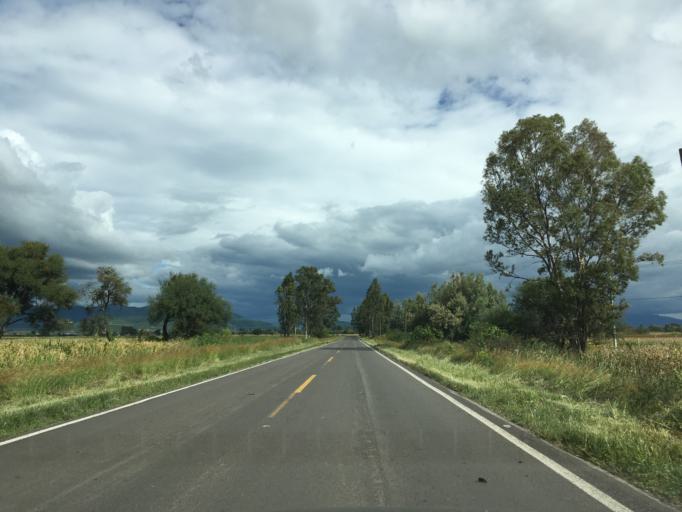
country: MX
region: Michoacan
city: Santa Ana Maya
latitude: 20.0388
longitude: -101.0578
